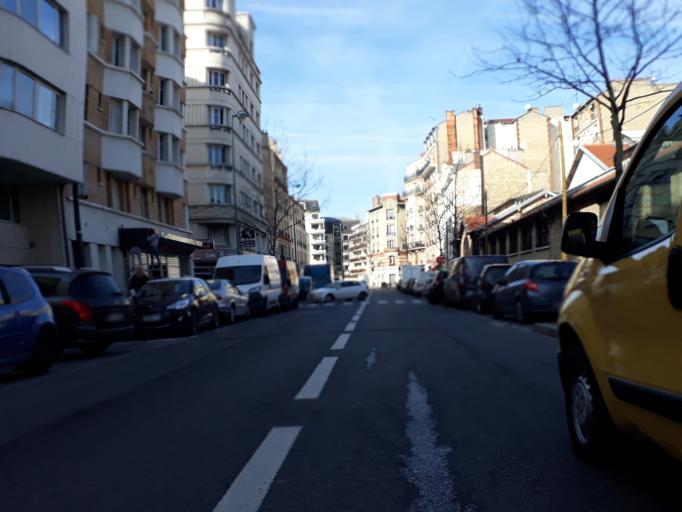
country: FR
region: Ile-de-France
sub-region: Departement des Hauts-de-Seine
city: Asnieres-sur-Seine
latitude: 48.9141
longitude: 2.2949
